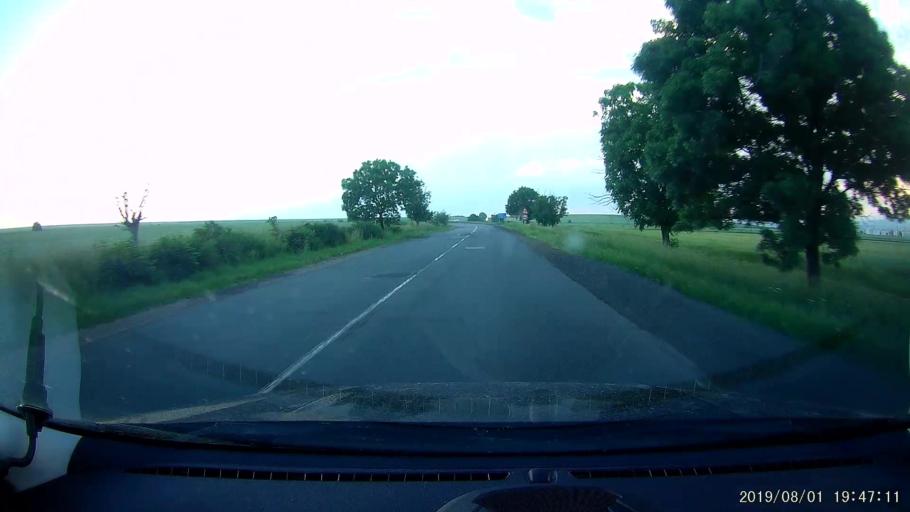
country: BG
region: Burgas
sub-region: Obshtina Karnobat
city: Karnobat
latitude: 42.6509
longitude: 26.9602
